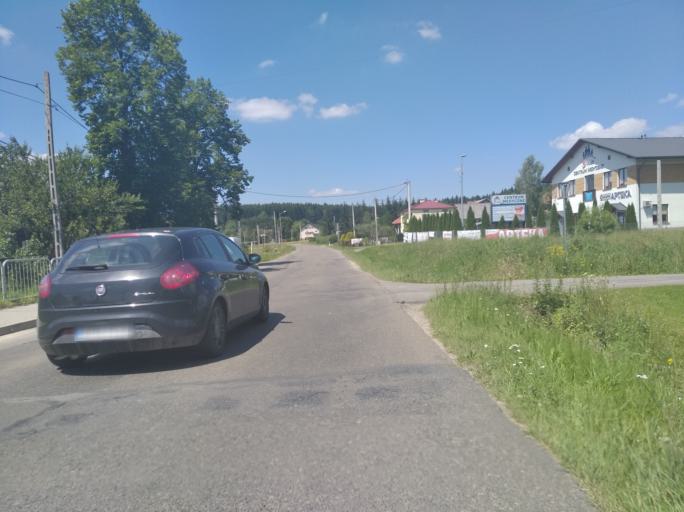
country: PL
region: Subcarpathian Voivodeship
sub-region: Powiat brzozowski
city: Dydnia
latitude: 49.6970
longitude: 22.1468
